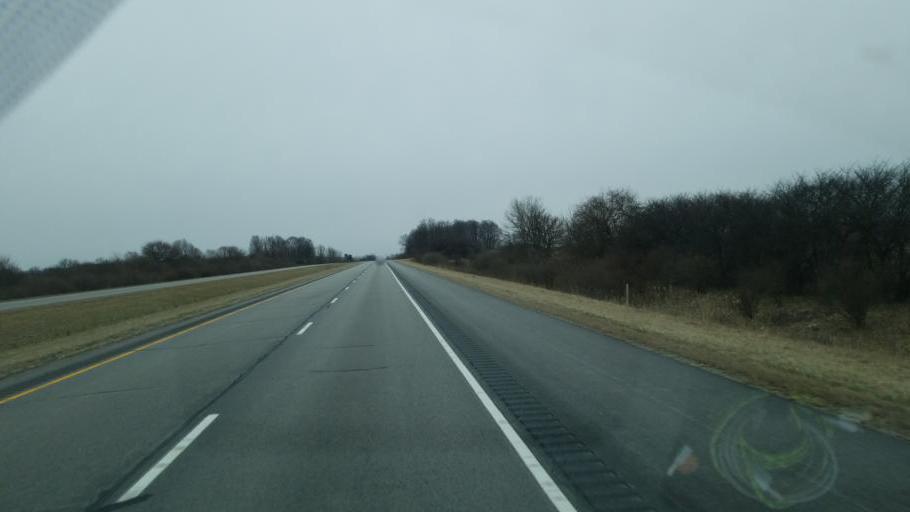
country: US
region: Indiana
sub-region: Marshall County
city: Argos
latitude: 41.1833
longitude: -86.2477
